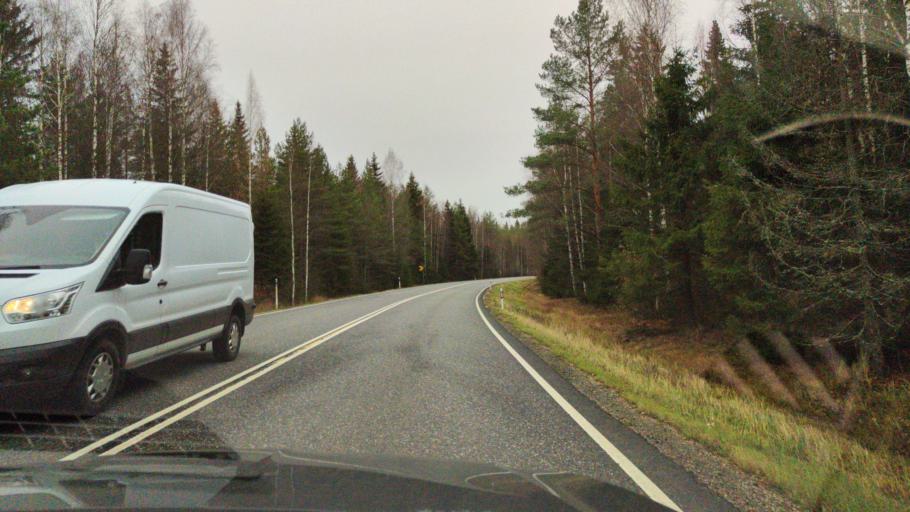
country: FI
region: Varsinais-Suomi
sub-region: Loimaa
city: Ylaene
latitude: 60.7396
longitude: 22.4265
